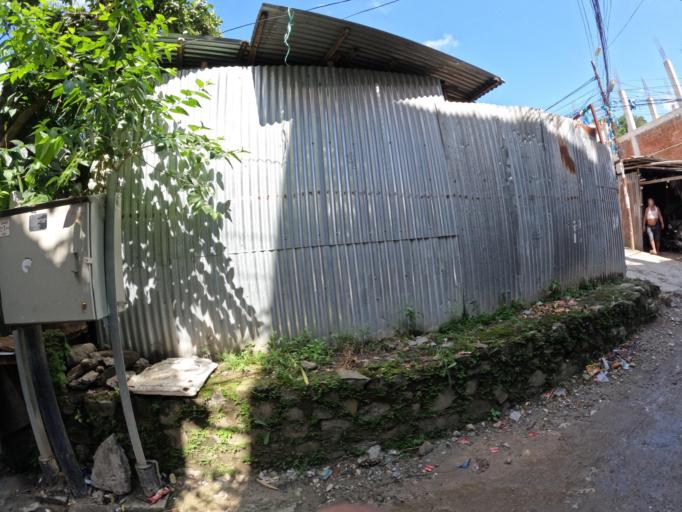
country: NP
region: Central Region
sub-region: Bagmati Zone
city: Kathmandu
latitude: 27.7448
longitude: 85.3313
